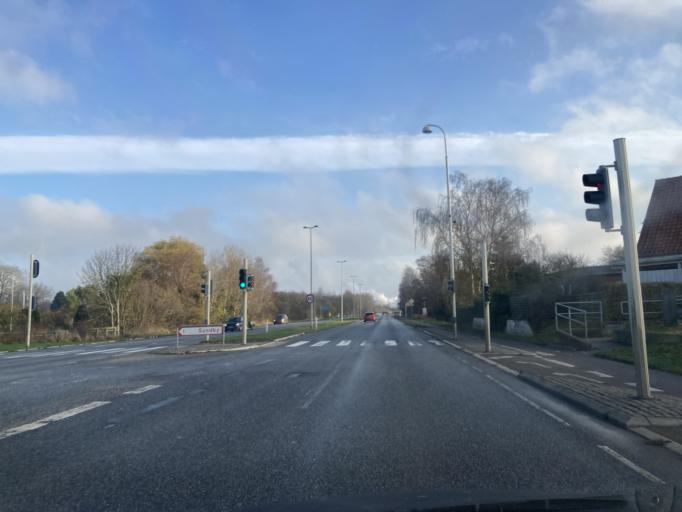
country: DK
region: Zealand
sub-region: Guldborgsund Kommune
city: Nykobing Falster
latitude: 54.7578
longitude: 11.8343
